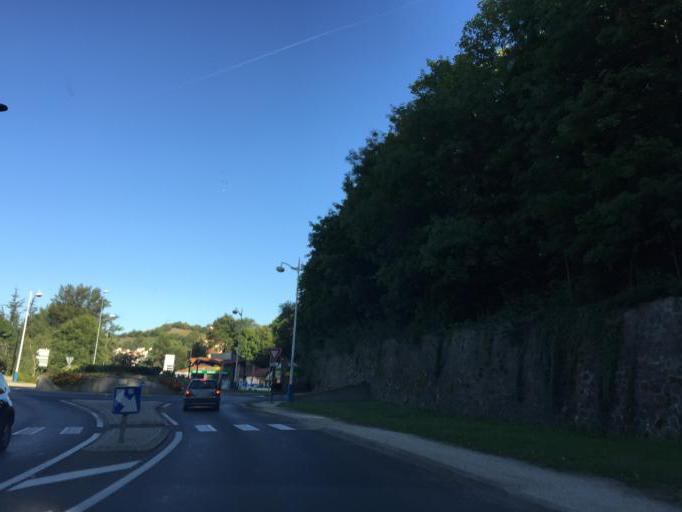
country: FR
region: Auvergne
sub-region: Departement de la Haute-Loire
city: Le Puy-en-Velay
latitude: 45.0498
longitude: 3.8870
